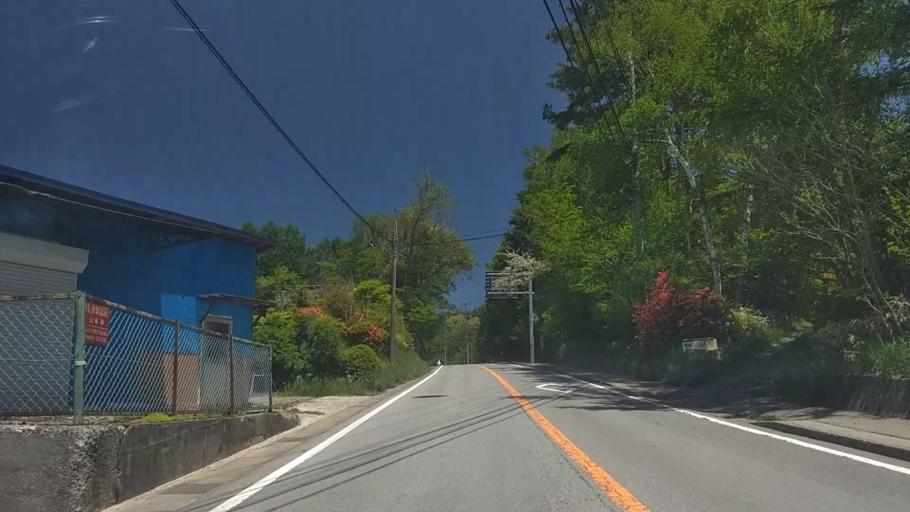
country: JP
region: Yamanashi
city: Nirasaki
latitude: 35.9074
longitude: 138.4444
